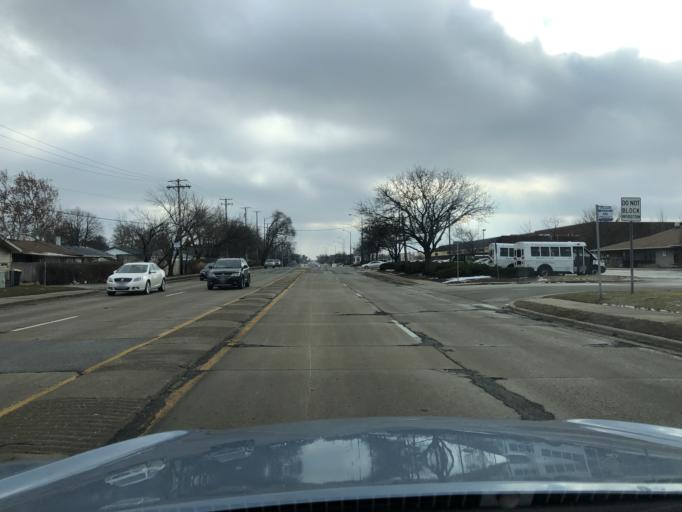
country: US
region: Illinois
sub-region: DuPage County
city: Itasca
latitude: 42.0068
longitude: -88.0039
